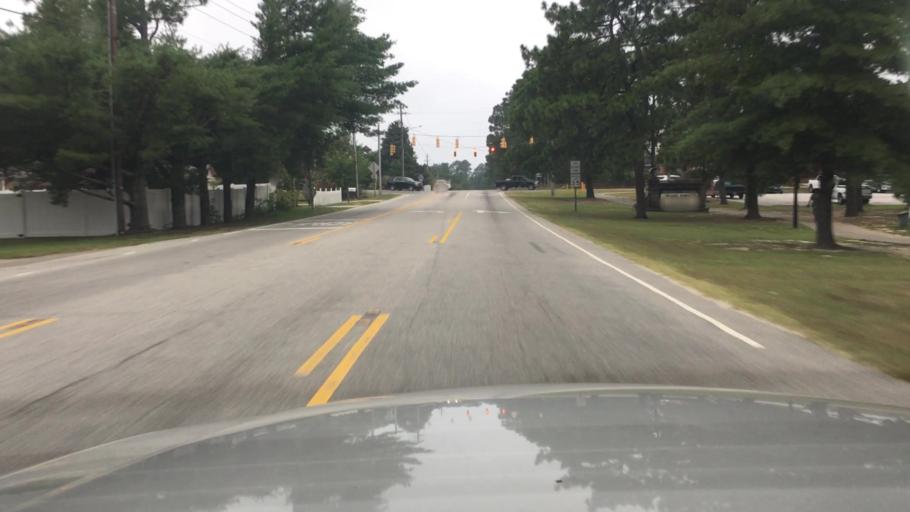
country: US
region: North Carolina
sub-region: Cumberland County
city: Hope Mills
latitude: 34.9726
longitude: -78.9585
